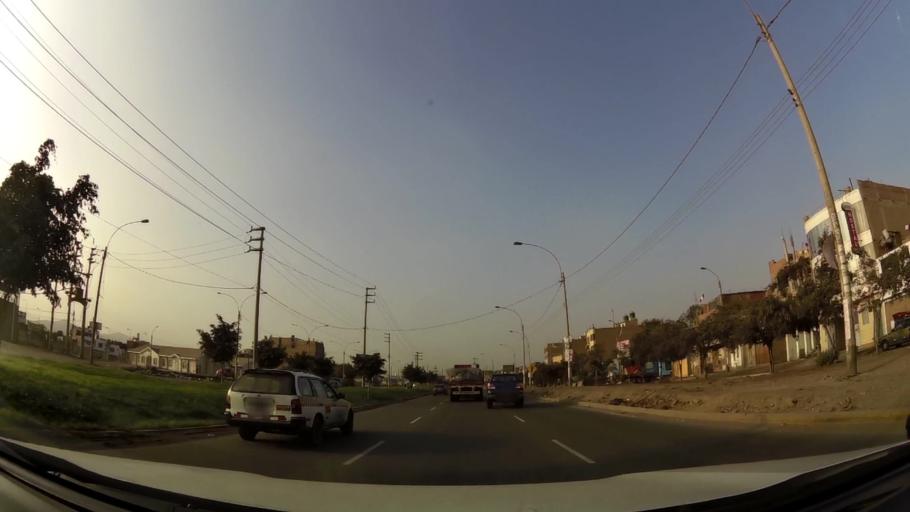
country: PE
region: Lima
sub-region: Lima
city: Independencia
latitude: -11.9726
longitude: -77.0865
